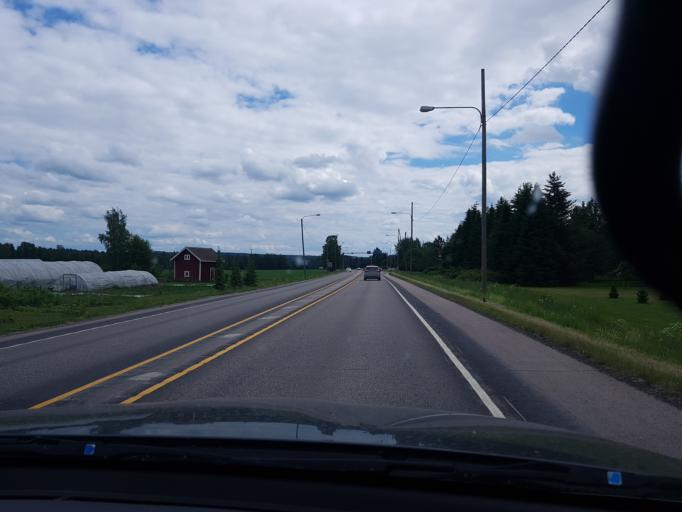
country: FI
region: Pirkanmaa
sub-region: Tampere
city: Paelkaene
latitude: 61.3426
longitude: 24.2673
